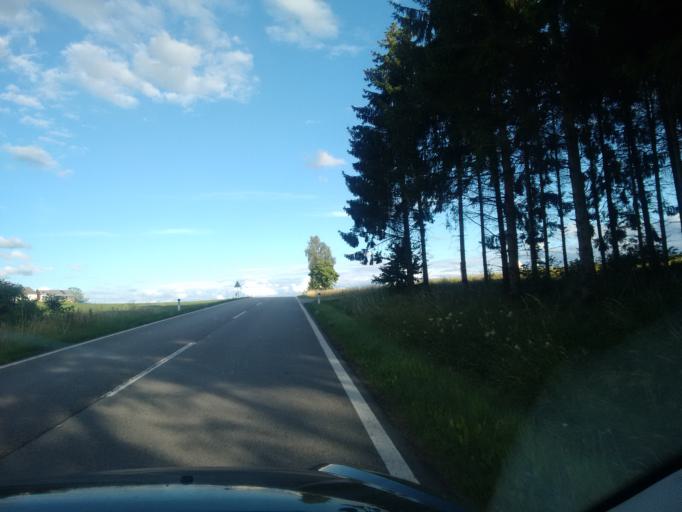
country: AT
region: Upper Austria
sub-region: Politischer Bezirk Urfahr-Umgebung
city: Gramastetten
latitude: 48.4139
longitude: 14.1643
